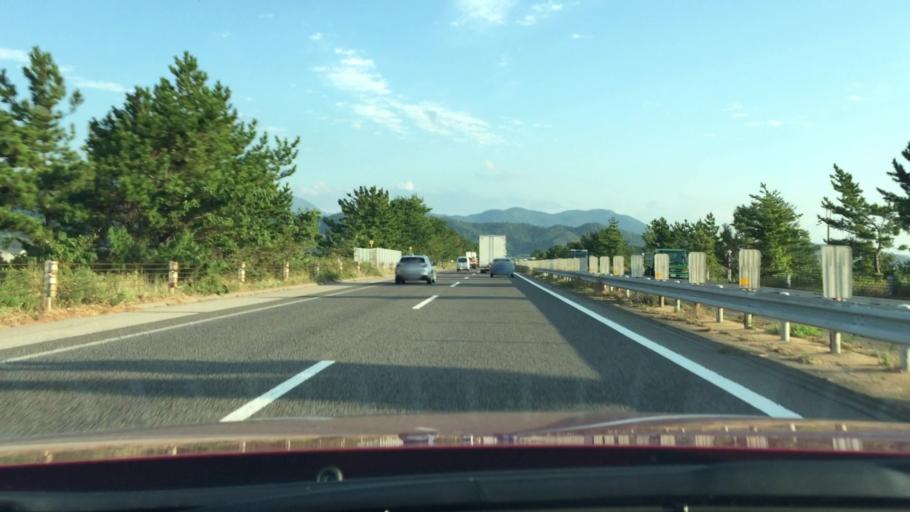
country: JP
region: Shiga Prefecture
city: Nagahama
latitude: 35.3745
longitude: 136.3032
